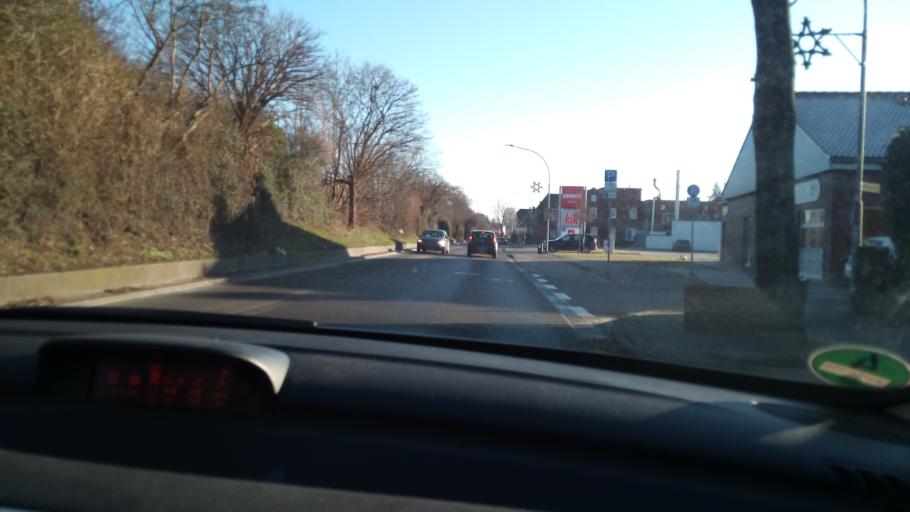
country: DE
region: Schleswig-Holstein
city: Buchen
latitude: 53.4780
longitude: 10.6179
